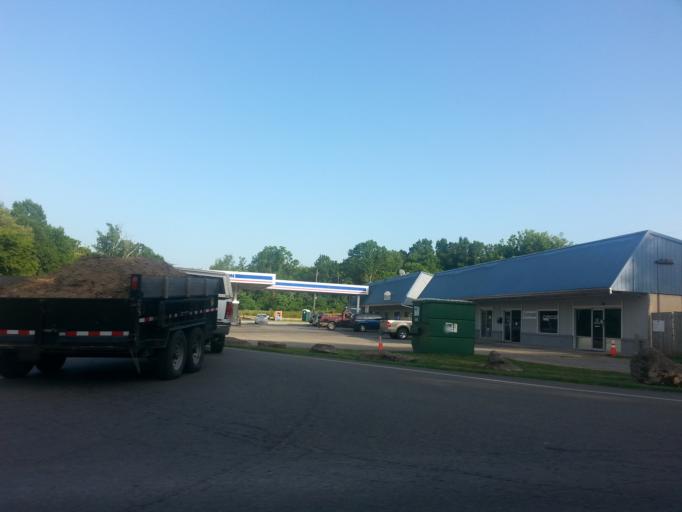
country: US
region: Tennessee
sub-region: Loudon County
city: Greenback
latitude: 35.7581
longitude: -84.1356
